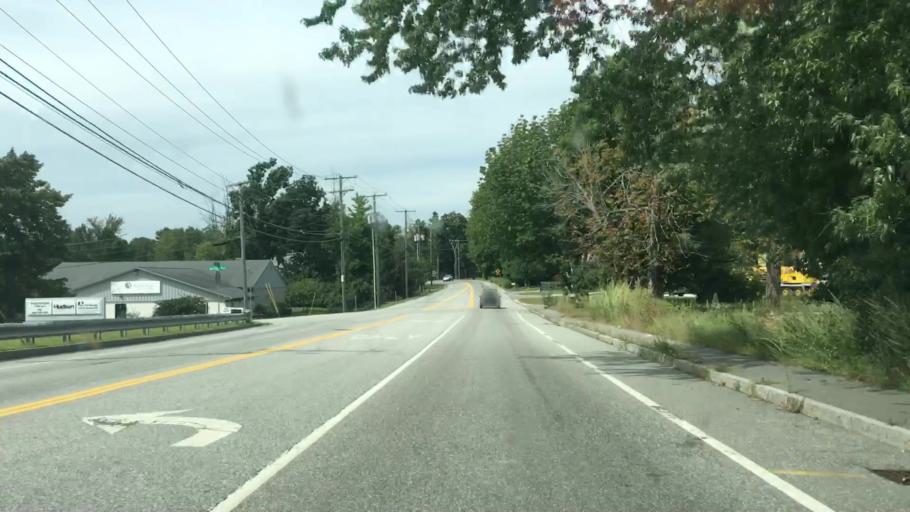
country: US
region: New Hampshire
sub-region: Strafford County
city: Dover
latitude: 43.1874
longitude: -70.8984
